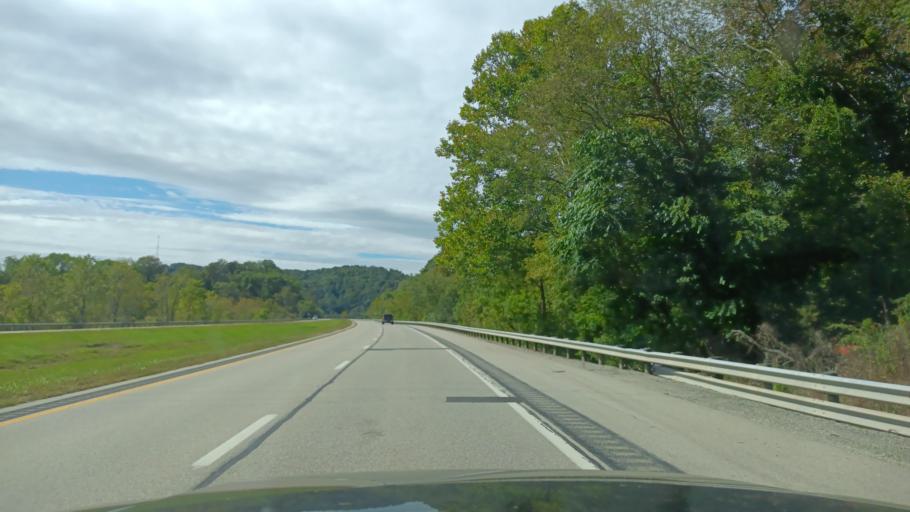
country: US
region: West Virginia
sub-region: Doddridge County
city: West Union
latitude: 39.2877
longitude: -80.7201
